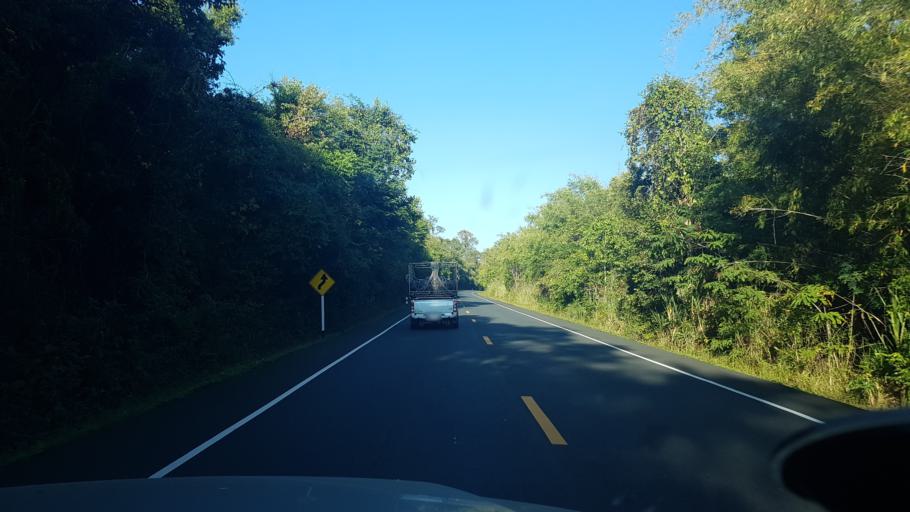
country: TH
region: Phetchabun
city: Nam Nao
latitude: 16.7025
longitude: 101.6110
